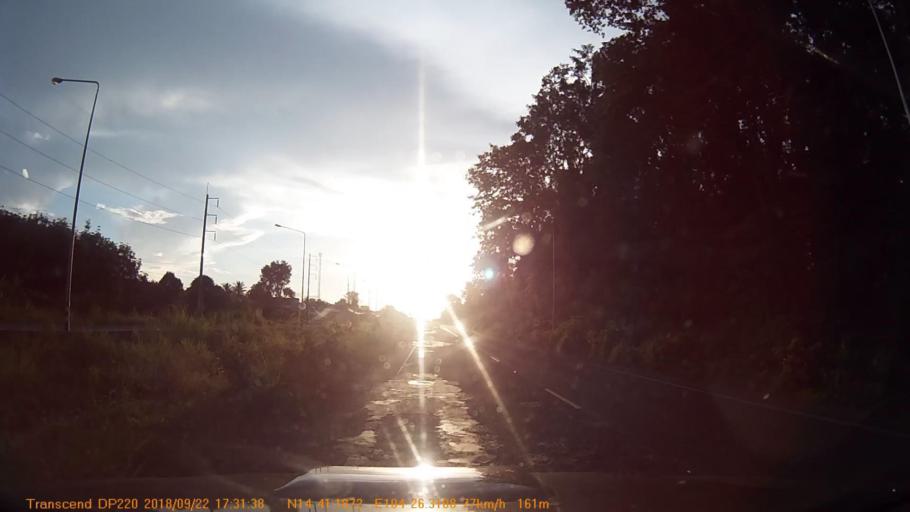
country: TH
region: Sisaket
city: Khun Han
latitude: 14.6865
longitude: 104.4380
